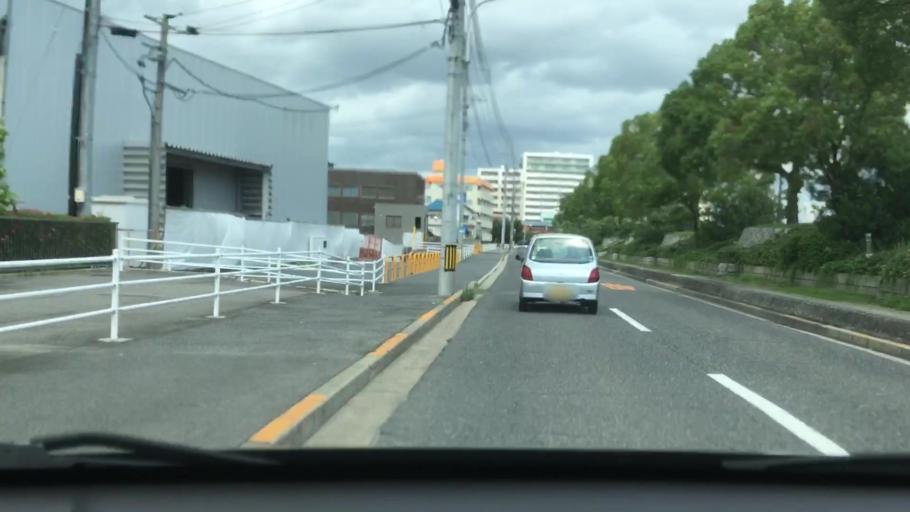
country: JP
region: Hiroshima
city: Hiroshima-shi
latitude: 34.3765
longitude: 132.4421
